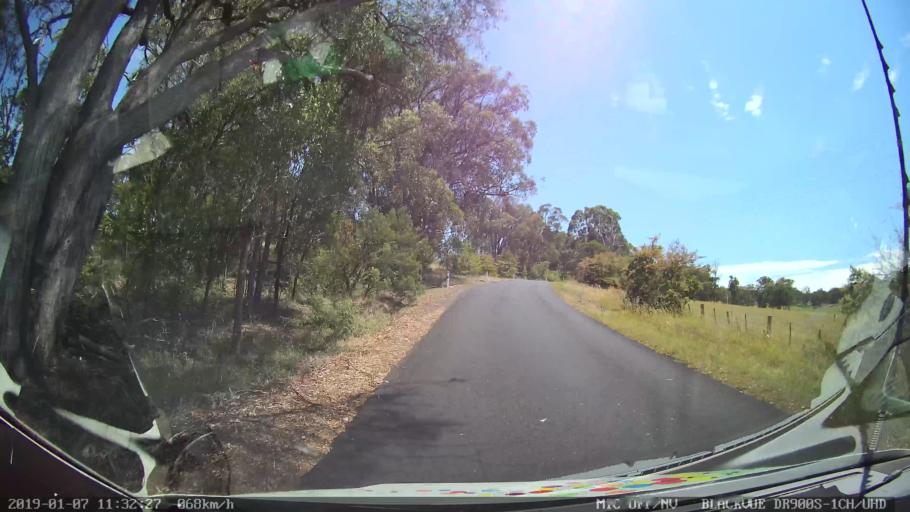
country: AU
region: New South Wales
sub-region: Armidale Dumaresq
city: Armidale
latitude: -30.4090
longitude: 151.5595
